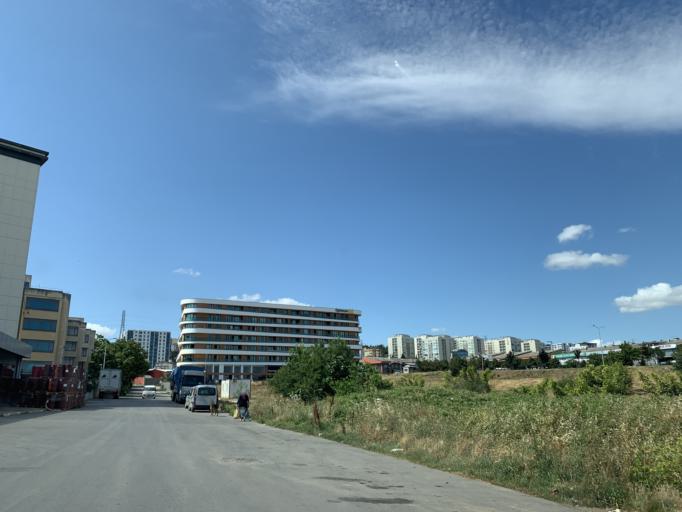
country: TR
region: Istanbul
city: Pendik
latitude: 40.8943
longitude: 29.2602
